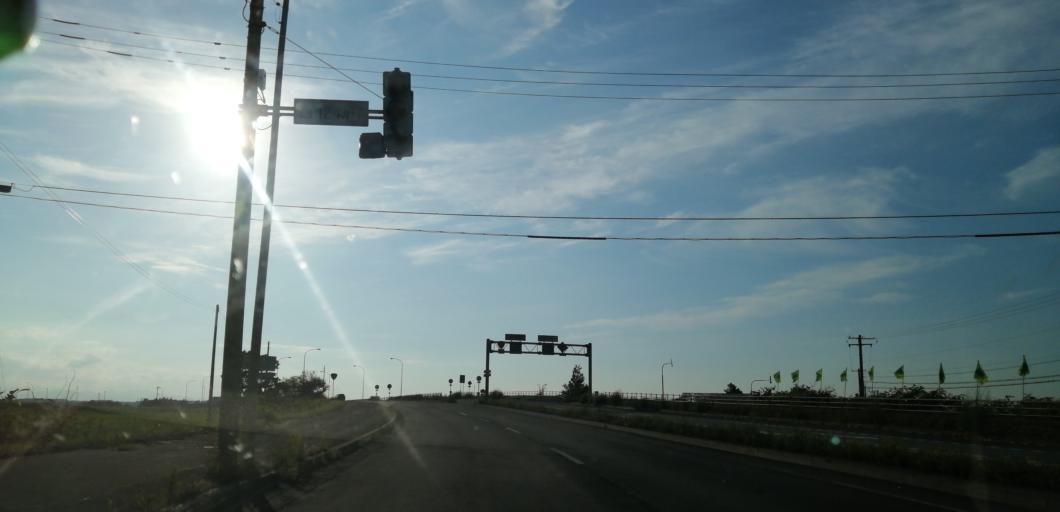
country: JP
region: Hokkaido
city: Kitahiroshima
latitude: 42.9969
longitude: 141.5889
